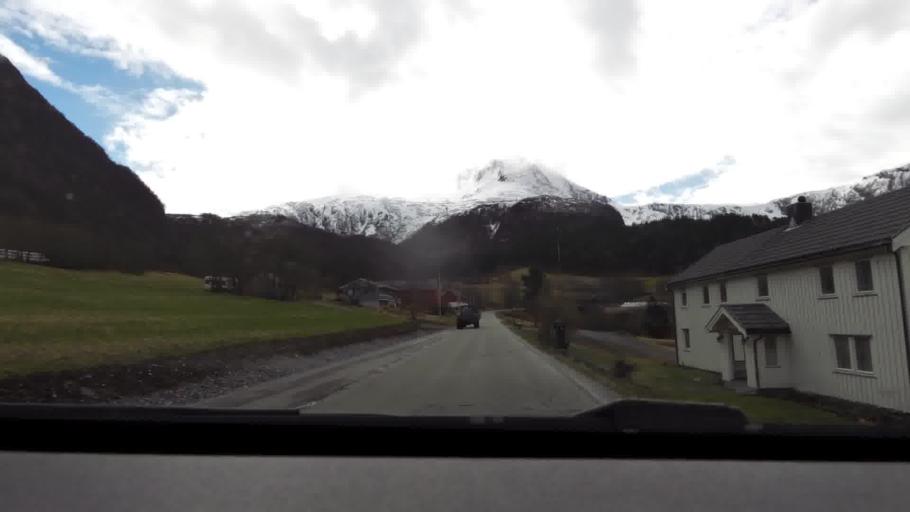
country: NO
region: More og Romsdal
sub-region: Gjemnes
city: Batnfjordsora
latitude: 62.9325
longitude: 7.6049
